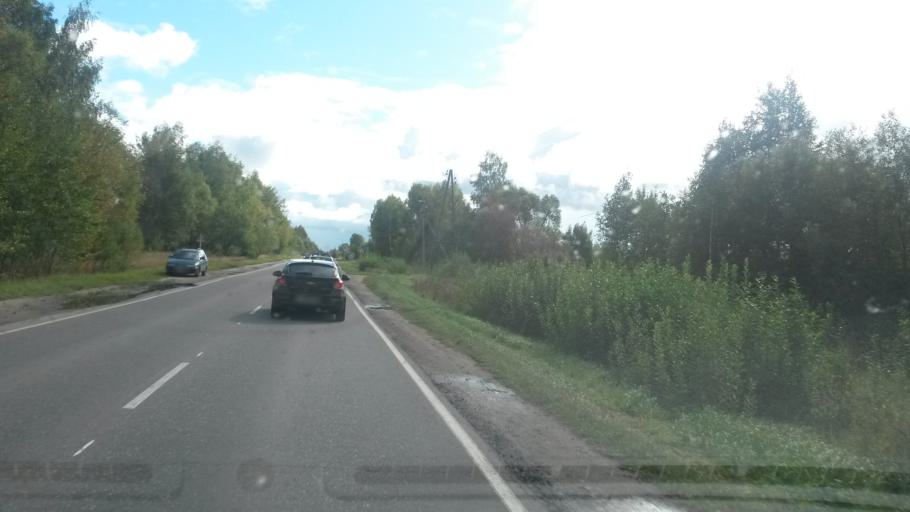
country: RU
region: Ivanovo
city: Zavolzhsk
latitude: 57.5060
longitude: 42.0984
